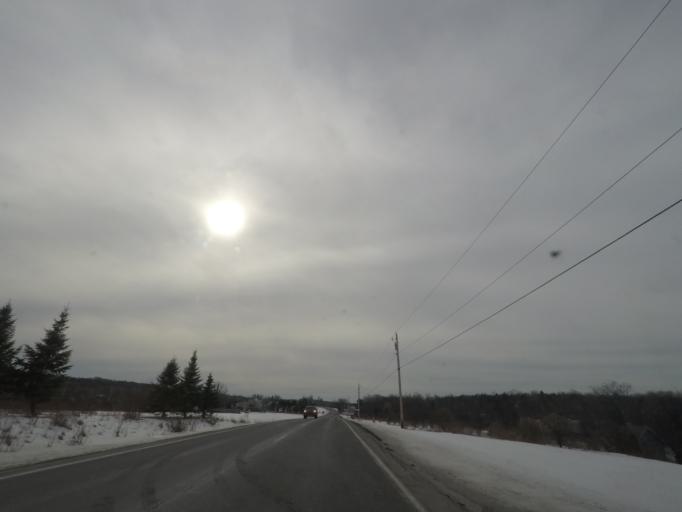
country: US
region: New York
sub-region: Albany County
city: Altamont
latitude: 42.6913
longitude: -74.0629
